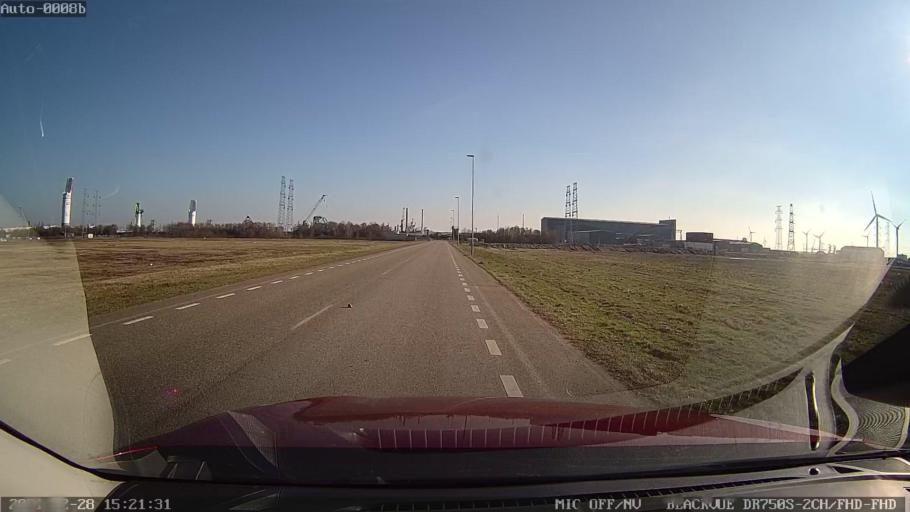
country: NL
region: Zeeland
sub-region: Gemeente Borsele
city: Borssele
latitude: 51.4600
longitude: 3.7109
